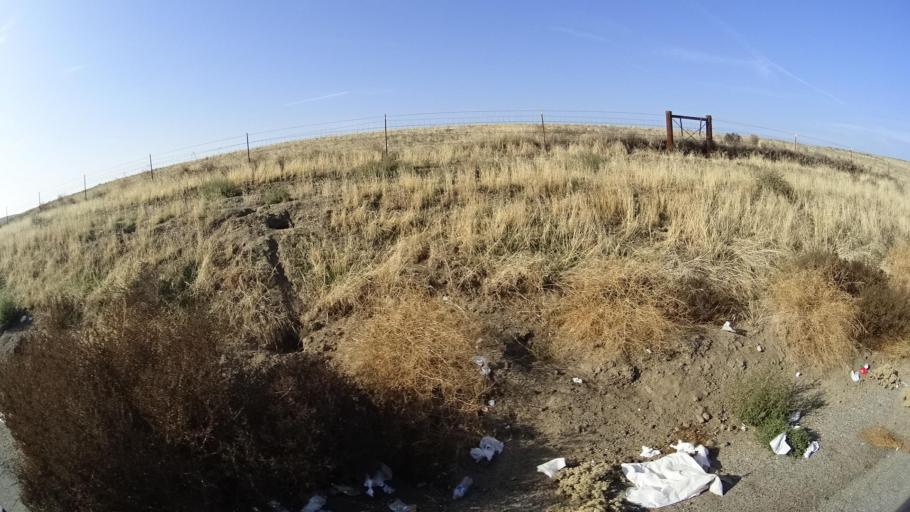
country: US
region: California
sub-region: Tulare County
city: Richgrove
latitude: 35.6289
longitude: -119.0320
